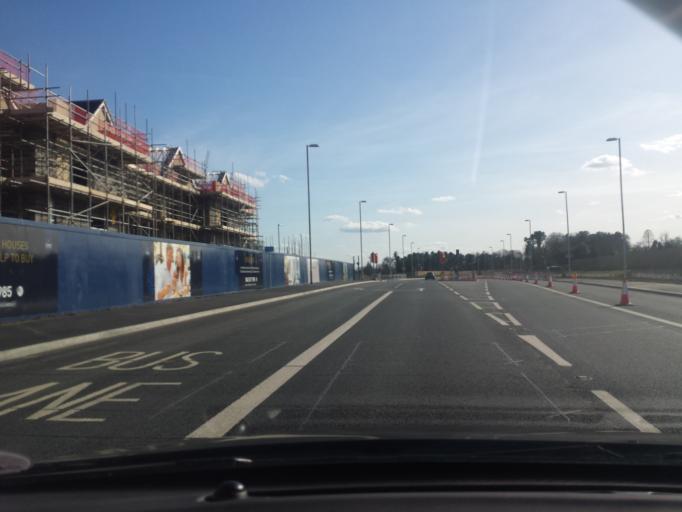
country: GB
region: England
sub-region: Essex
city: Colchester
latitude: 51.9202
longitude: 0.9038
